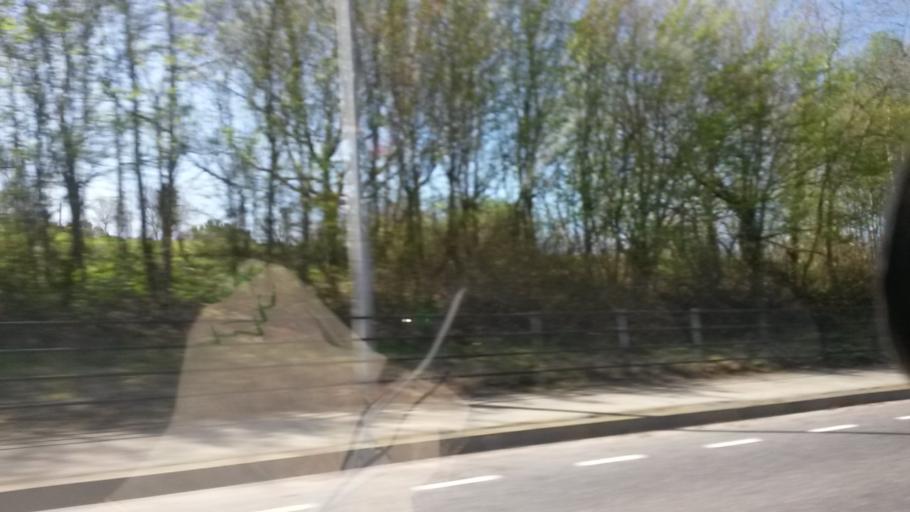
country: IE
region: Munster
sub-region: County Cork
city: Cork
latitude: 51.8942
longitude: -8.5212
